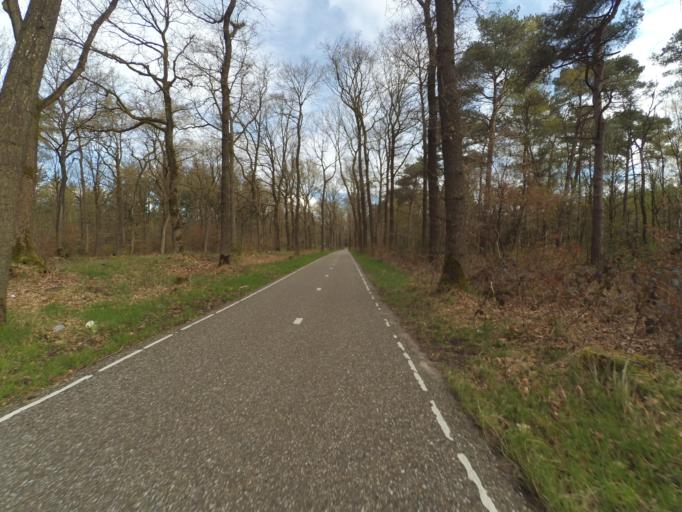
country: NL
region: Gelderland
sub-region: Gemeente Nunspeet
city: Nunspeet
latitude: 52.3382
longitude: 5.7898
